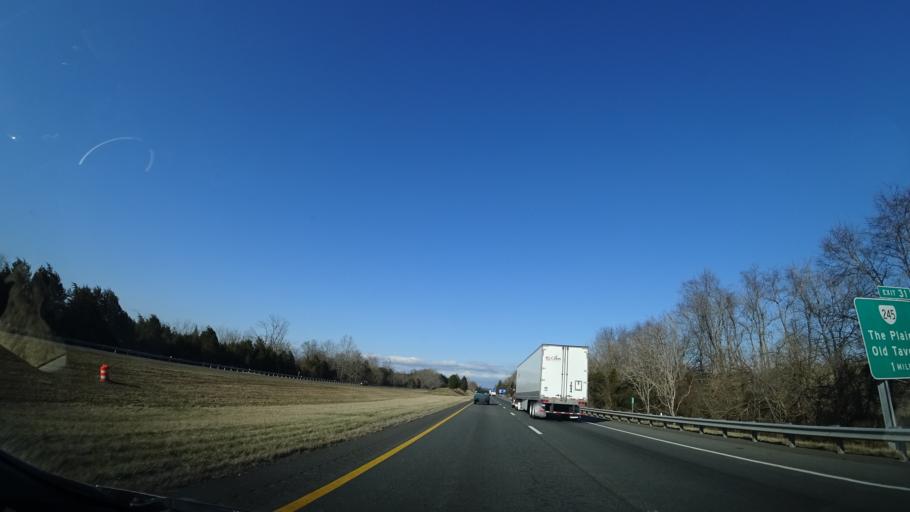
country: US
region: Virginia
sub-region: Fauquier County
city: New Baltimore
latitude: 38.8478
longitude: -77.7647
